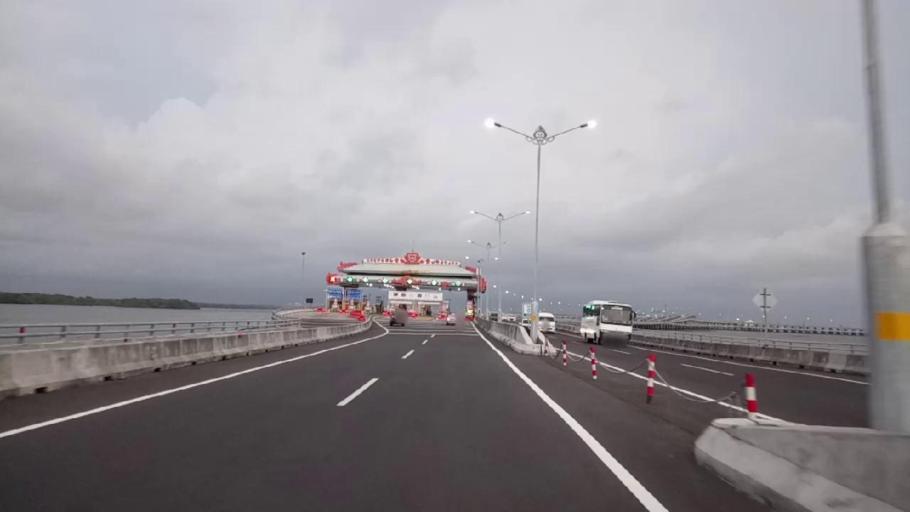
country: ID
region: Bali
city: Kelanabian
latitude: -8.7448
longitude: 115.1868
